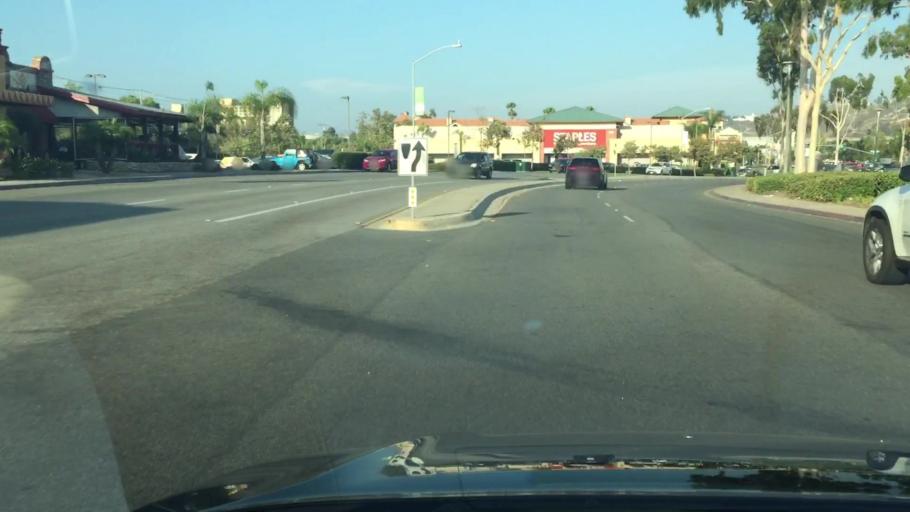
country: US
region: California
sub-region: San Diego County
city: San Diego
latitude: 32.7708
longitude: -117.1467
